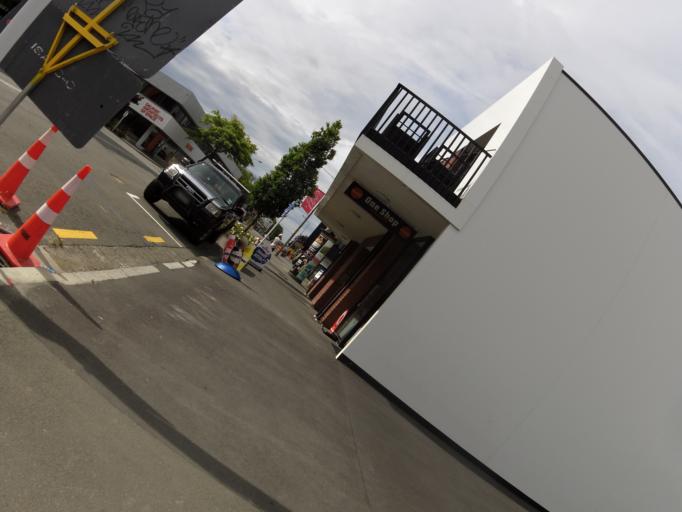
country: NZ
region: Canterbury
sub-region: Christchurch City
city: Christchurch
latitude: -43.5258
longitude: 172.6367
